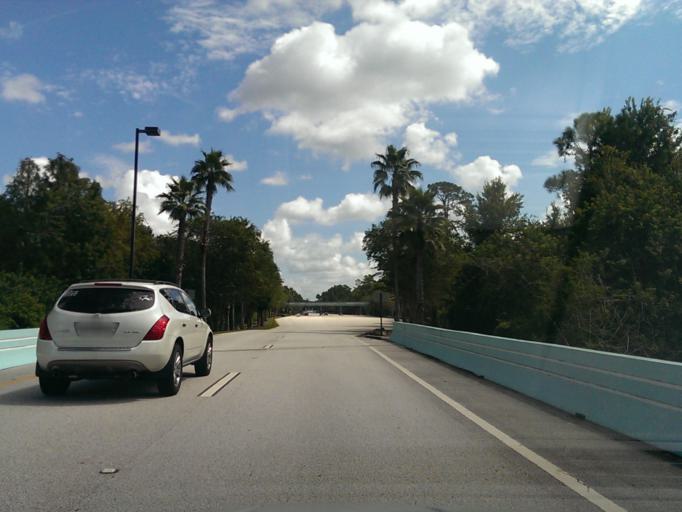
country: US
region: Florida
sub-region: Osceola County
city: Celebration
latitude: 28.3523
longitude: -81.5623
